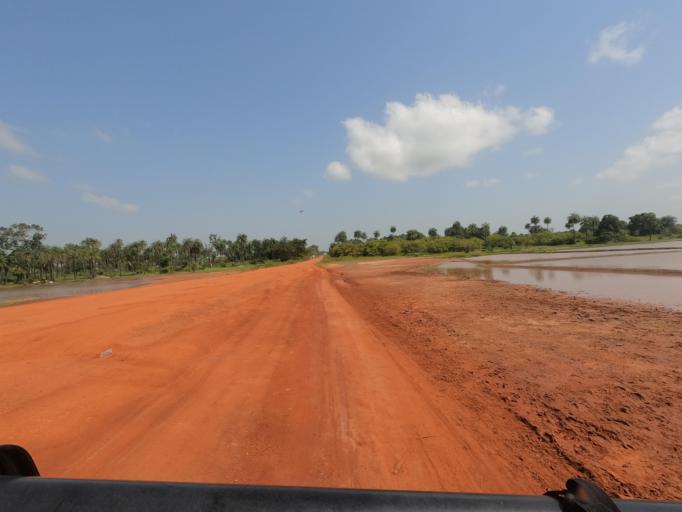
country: GW
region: Cacheu
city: Canchungo
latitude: 12.2760
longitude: -15.7867
